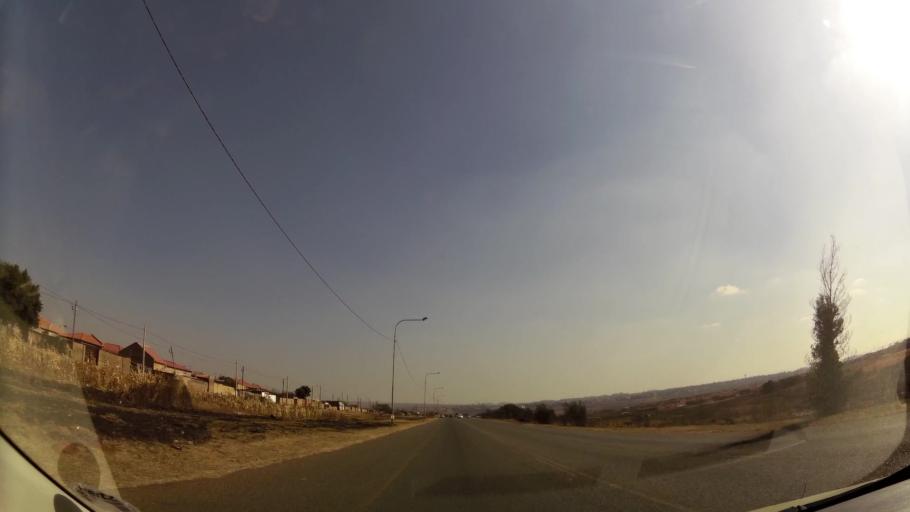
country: ZA
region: Gauteng
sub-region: West Rand District Municipality
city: Randfontein
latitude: -26.1737
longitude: 27.7792
